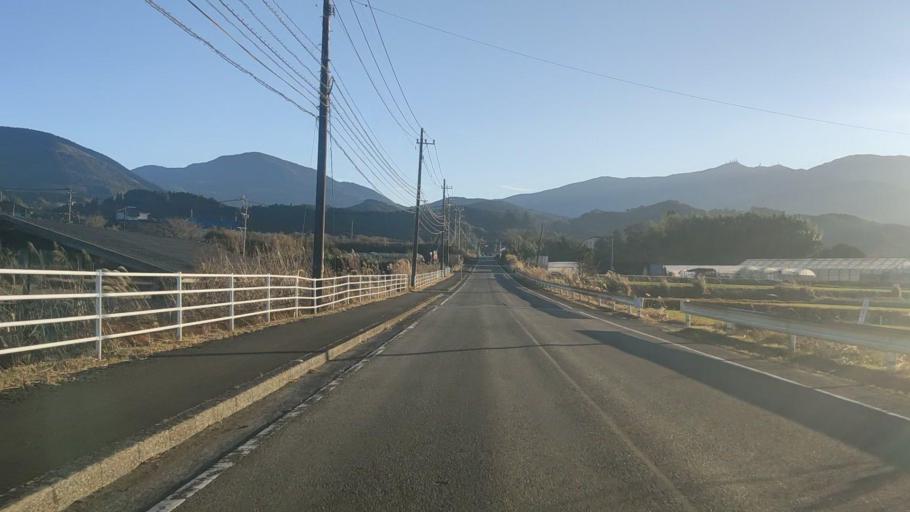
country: JP
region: Miyazaki
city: Miyazaki-shi
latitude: 31.8278
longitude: 131.2987
